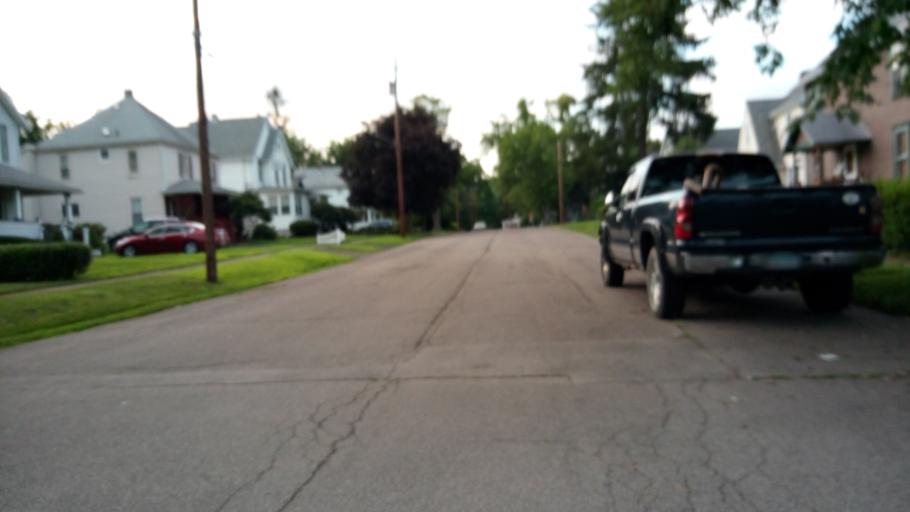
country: US
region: New York
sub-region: Chemung County
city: West Elmira
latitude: 42.0766
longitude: -76.8402
